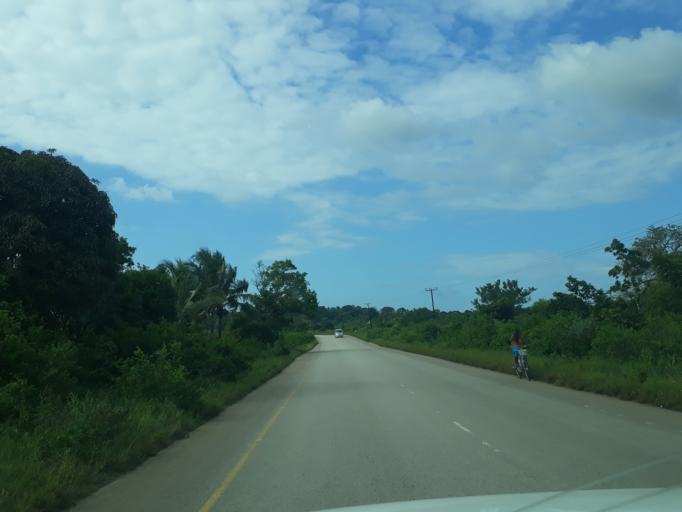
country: TZ
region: Zanzibar North
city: Kijini
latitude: -5.8377
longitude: 39.2873
